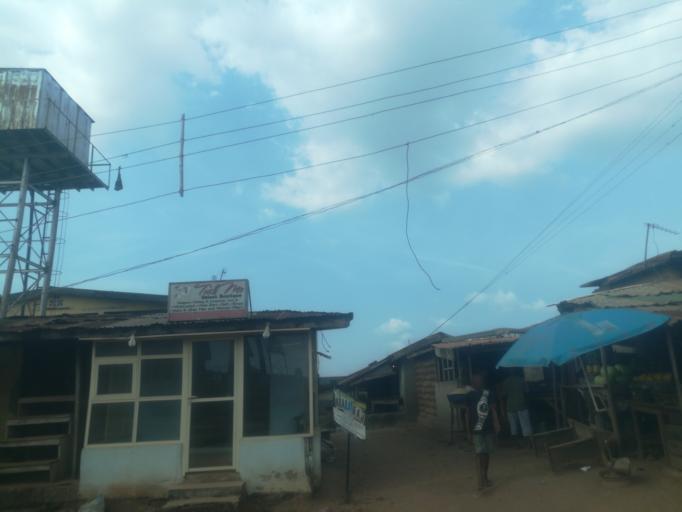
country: NG
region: Ogun
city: Abeokuta
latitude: 7.1185
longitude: 3.3216
